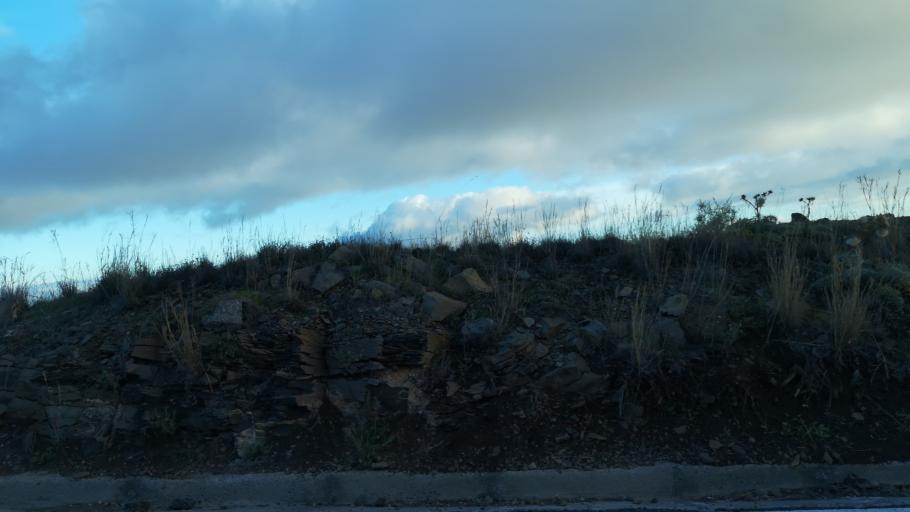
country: ES
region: Canary Islands
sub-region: Provincia de Santa Cruz de Tenerife
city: Alajero
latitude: 28.0456
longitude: -17.2335
